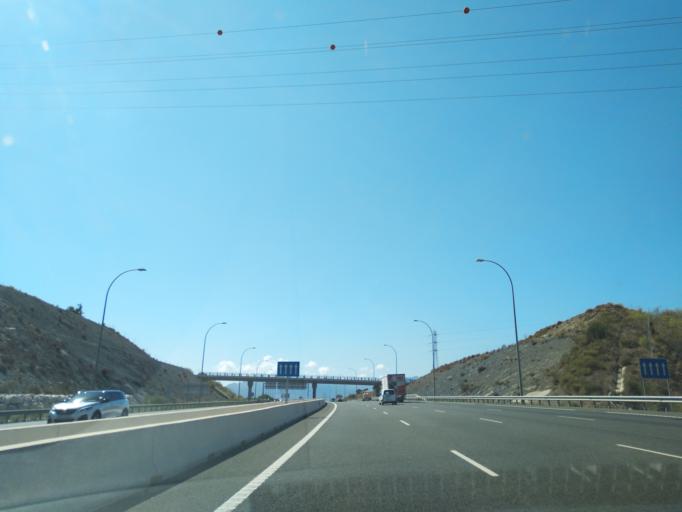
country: ES
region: Andalusia
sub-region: Provincia de Malaga
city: Malaga
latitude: 36.7445
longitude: -4.5017
